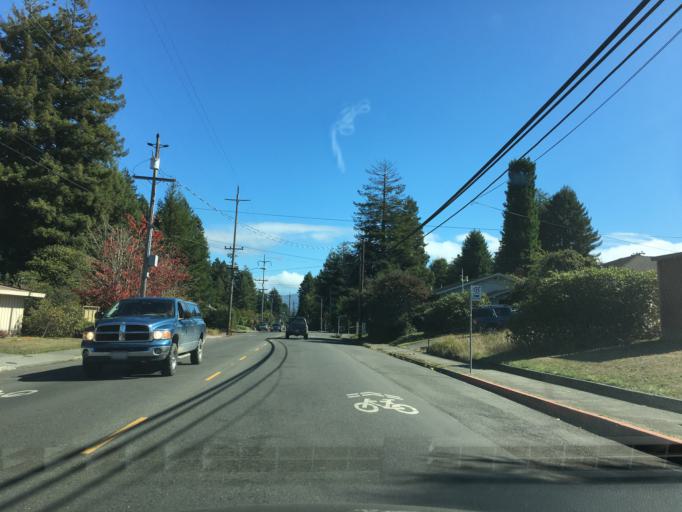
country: US
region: California
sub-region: Humboldt County
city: Cutten
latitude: 40.7804
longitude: -124.1470
